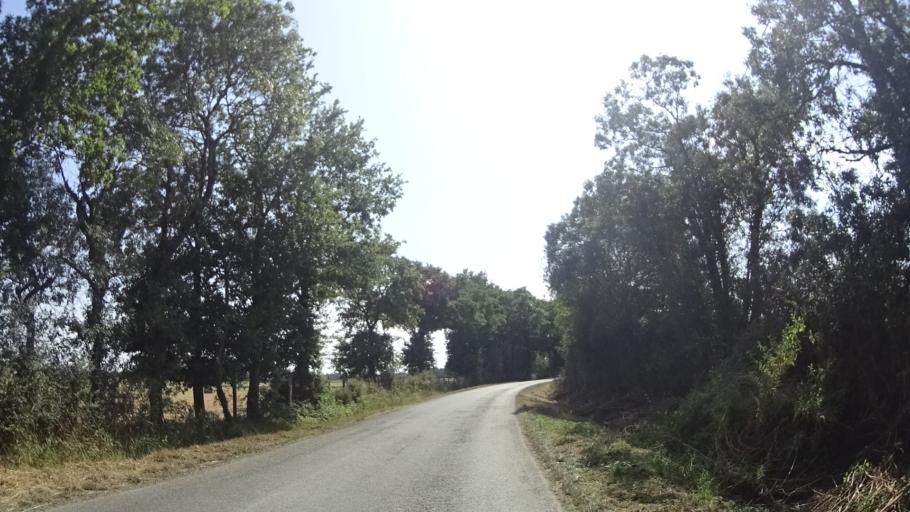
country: FR
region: Pays de la Loire
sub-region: Departement de la Loire-Atlantique
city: Prinquiau
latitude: 47.3448
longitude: -2.0050
